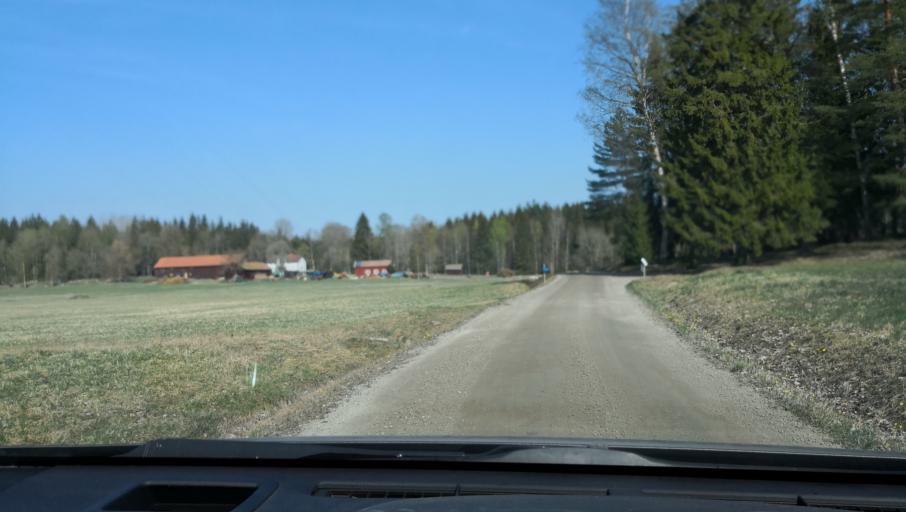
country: SE
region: Uppsala
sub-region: Heby Kommun
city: Heby
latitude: 60.0103
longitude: 16.7329
